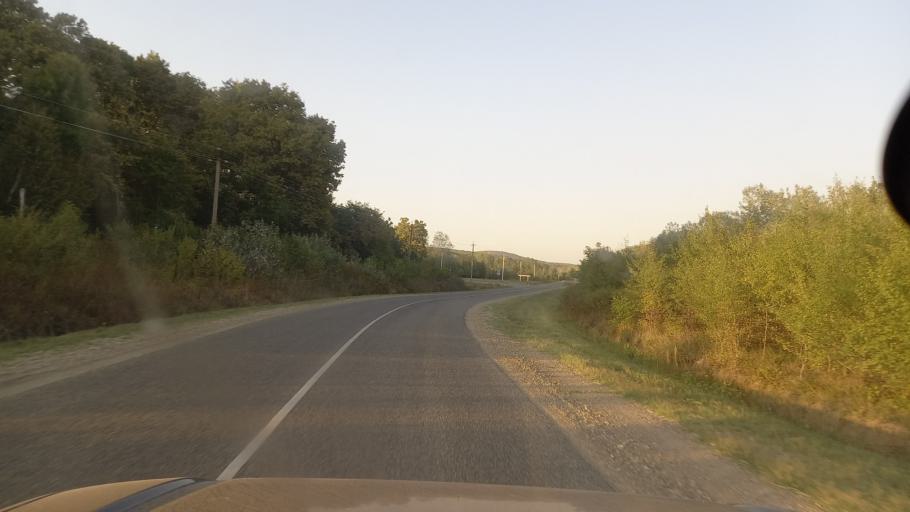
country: RU
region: Krasnodarskiy
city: Smolenskaya
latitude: 44.7523
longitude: 38.7629
